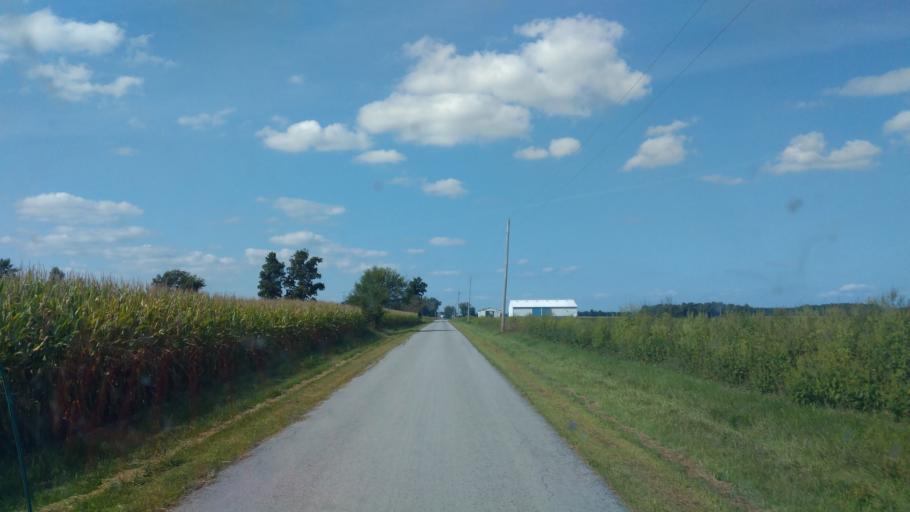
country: US
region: Ohio
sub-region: Hardin County
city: Forest
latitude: 40.7179
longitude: -83.4779
